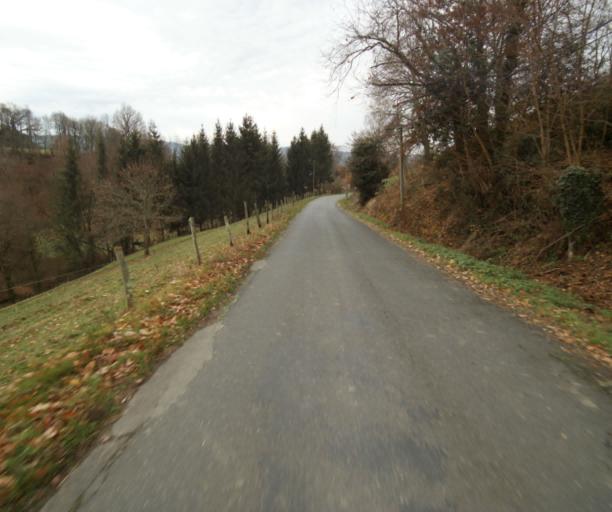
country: FR
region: Limousin
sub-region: Departement de la Correze
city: Tulle
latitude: 45.2484
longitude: 1.7358
